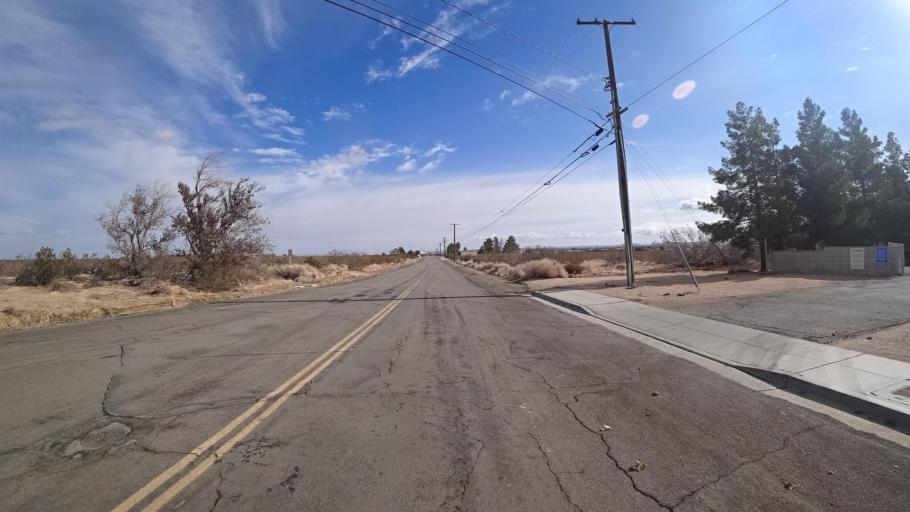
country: US
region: California
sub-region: Kern County
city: Mojave
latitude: 35.0611
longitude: -118.1925
